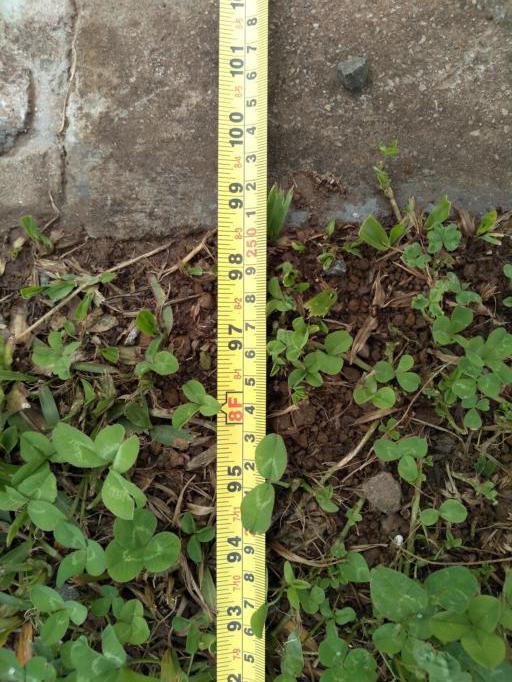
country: BR
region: Santa Catarina
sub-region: Curitibanos
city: Curitibanos
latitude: -27.2844
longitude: -50.5369
